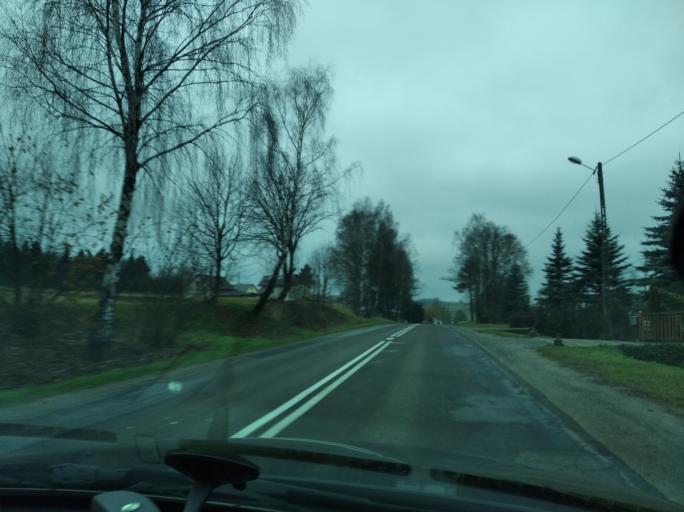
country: PL
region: Subcarpathian Voivodeship
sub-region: Powiat przeworski
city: Jawornik Polski
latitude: 49.8666
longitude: 22.2459
